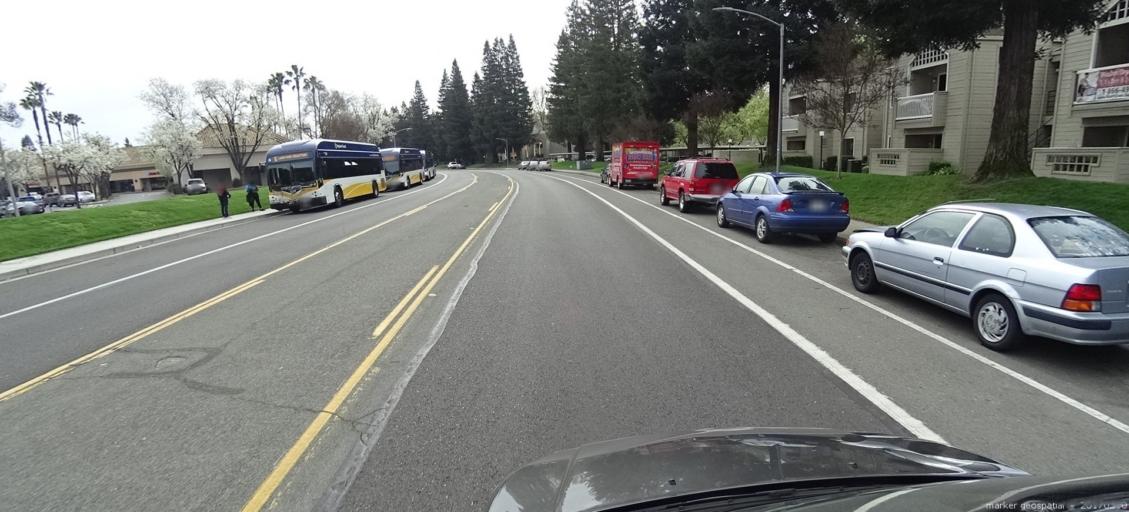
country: US
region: California
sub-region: Sacramento County
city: Parkway
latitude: 38.4861
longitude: -121.5364
